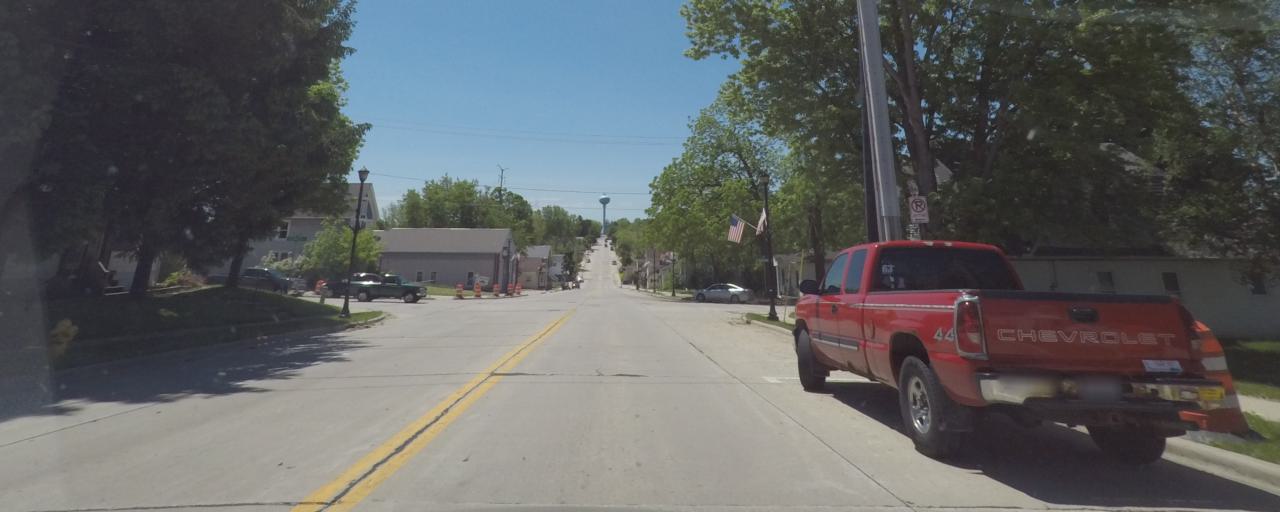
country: US
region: Wisconsin
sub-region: Washington County
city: West Bend
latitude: 43.4437
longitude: -88.1792
